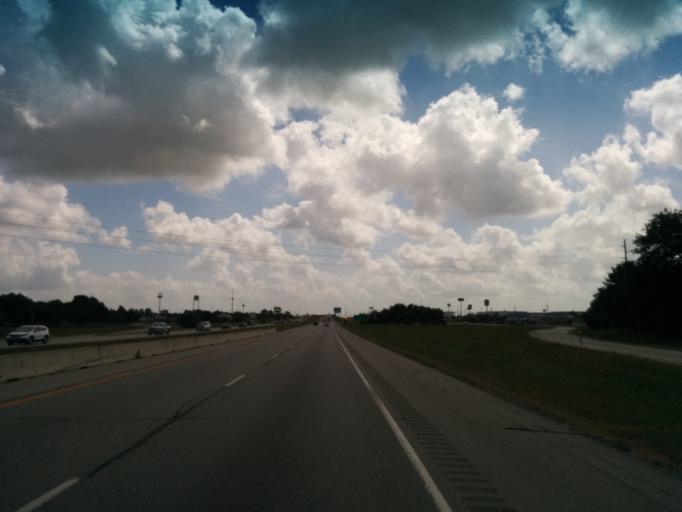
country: US
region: Texas
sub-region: Austin County
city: Sealy
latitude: 29.7621
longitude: -96.1601
